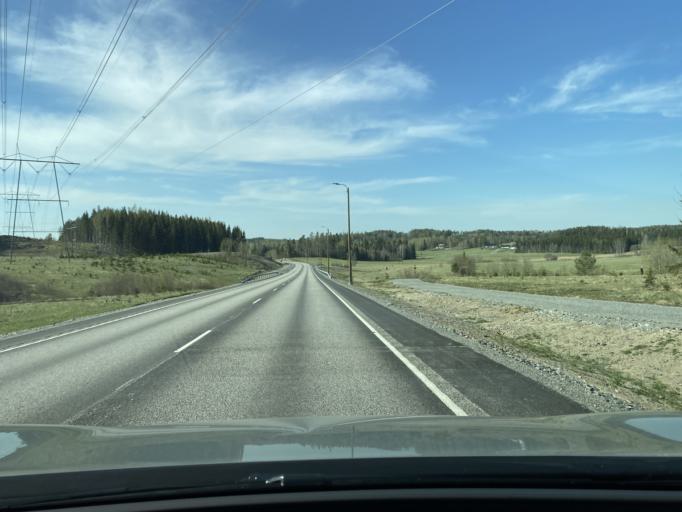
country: FI
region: Uusimaa
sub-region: Helsinki
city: Nurmijaervi
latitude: 60.4119
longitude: 24.7491
